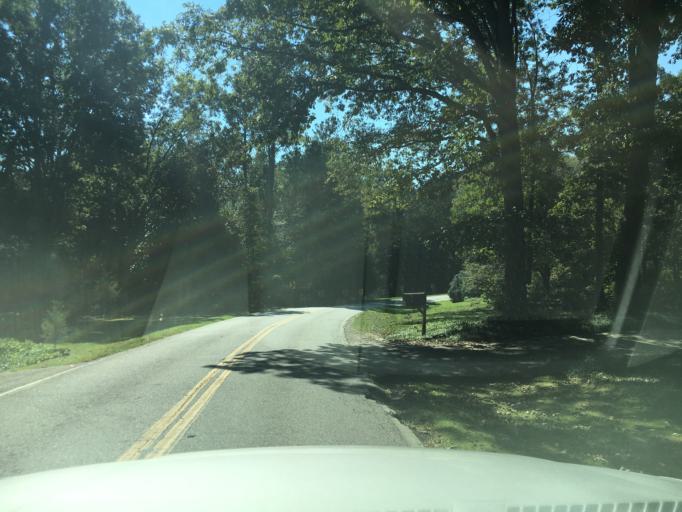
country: US
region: South Carolina
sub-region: Greenville County
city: Taylors
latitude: 34.8989
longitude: -82.2728
